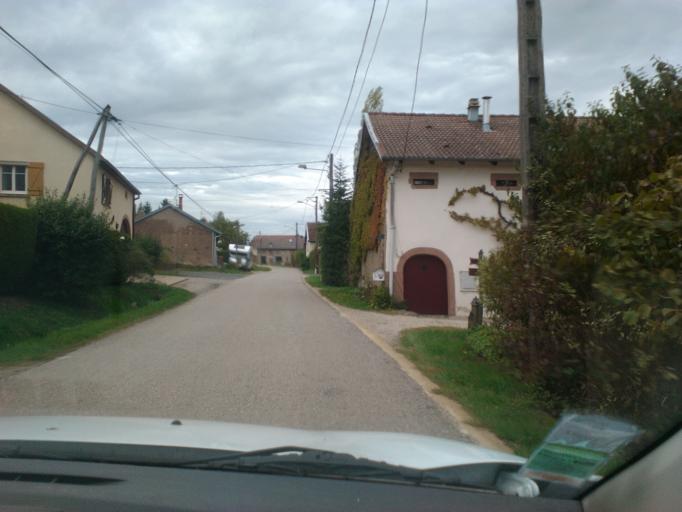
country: FR
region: Lorraine
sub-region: Departement des Vosges
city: Saint-Michel-sur-Meurthe
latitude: 48.3167
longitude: 6.8578
